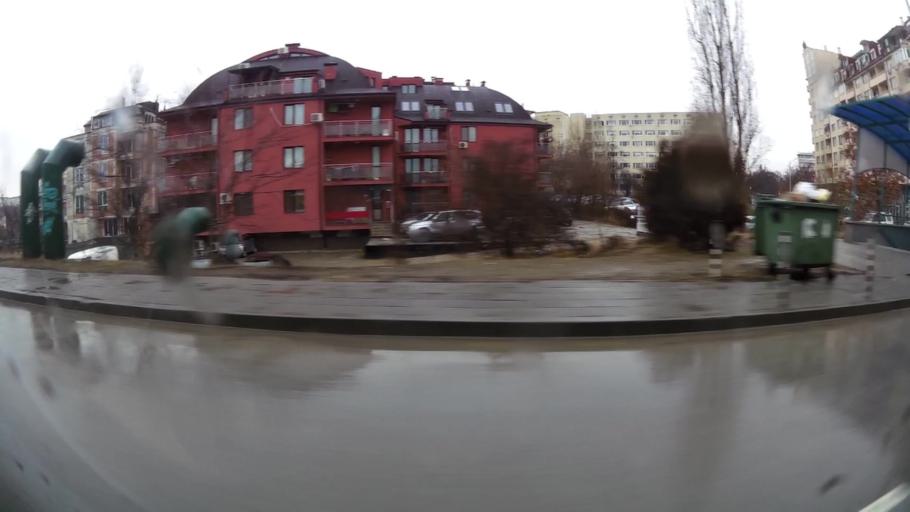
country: BG
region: Sofia-Capital
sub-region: Stolichna Obshtina
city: Sofia
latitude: 42.6583
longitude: 23.3646
